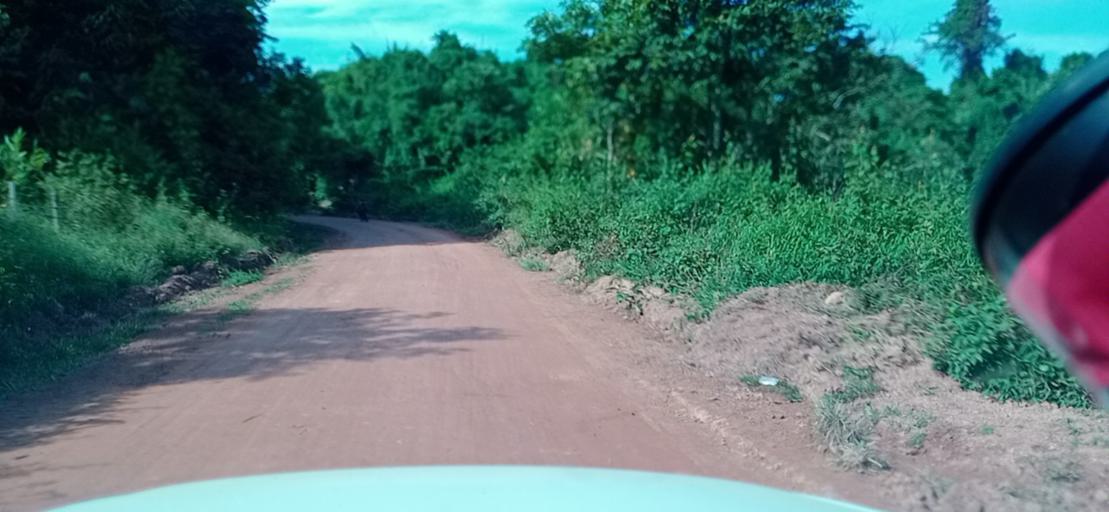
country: TH
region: Changwat Bueng Kan
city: Pak Khat
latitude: 18.6712
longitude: 103.1951
